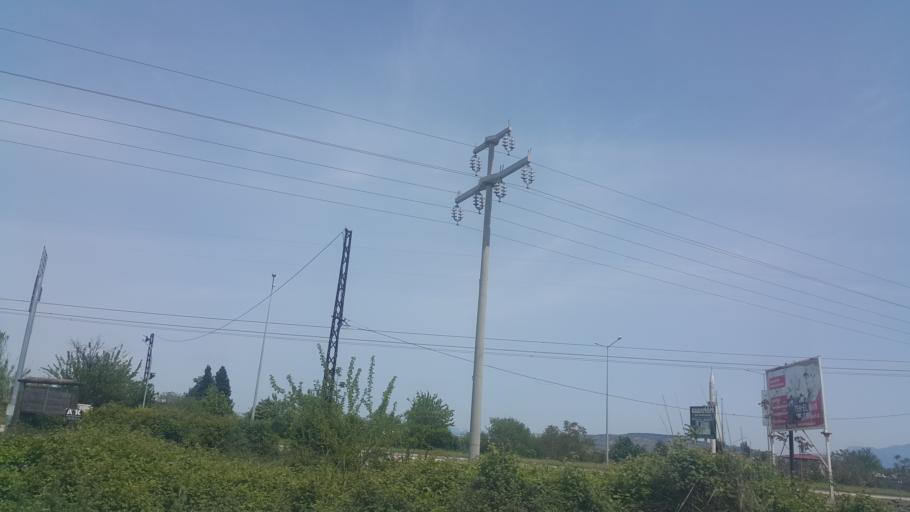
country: TR
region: Osmaniye
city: Toprakkale
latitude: 37.0561
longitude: 36.1228
